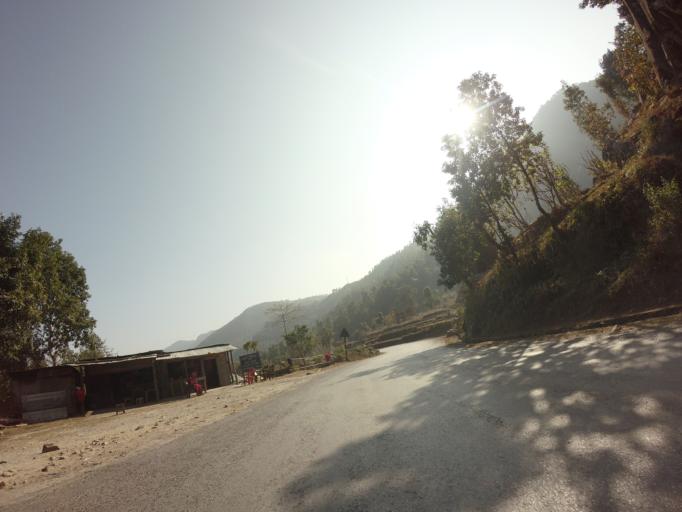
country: NP
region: Western Region
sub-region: Gandaki Zone
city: Pokhara
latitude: 28.1978
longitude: 83.8965
